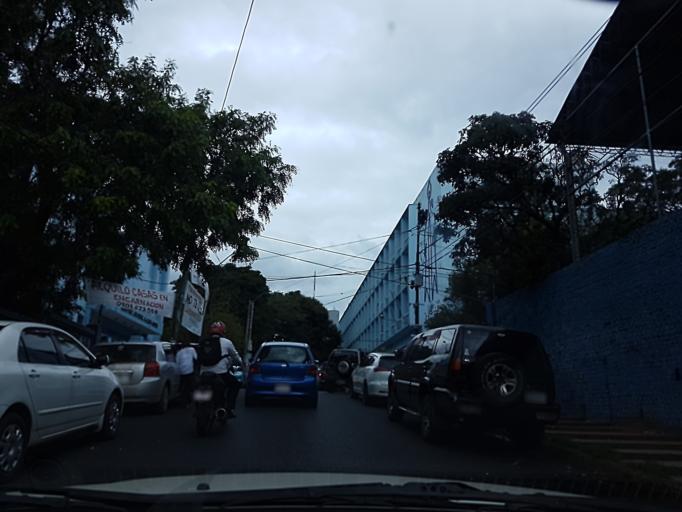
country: PY
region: Asuncion
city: Asuncion
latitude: -25.2931
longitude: -57.6271
